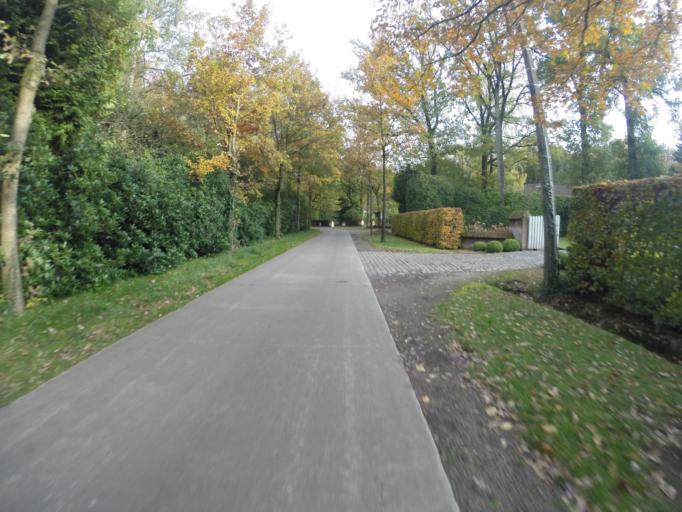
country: BE
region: Flanders
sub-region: Provincie Oost-Vlaanderen
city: Aalter
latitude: 51.0736
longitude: 3.4651
